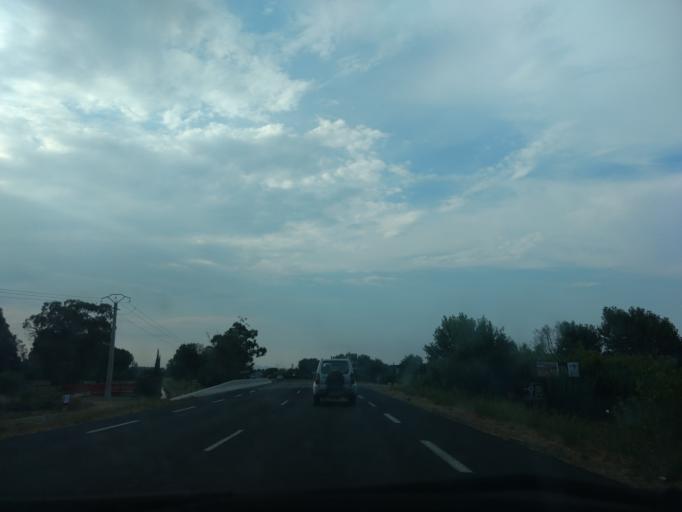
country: FR
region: Languedoc-Roussillon
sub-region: Departement des Pyrenees-Orientales
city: Saint-Cyprien-Plage
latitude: 42.6200
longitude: 3.0251
